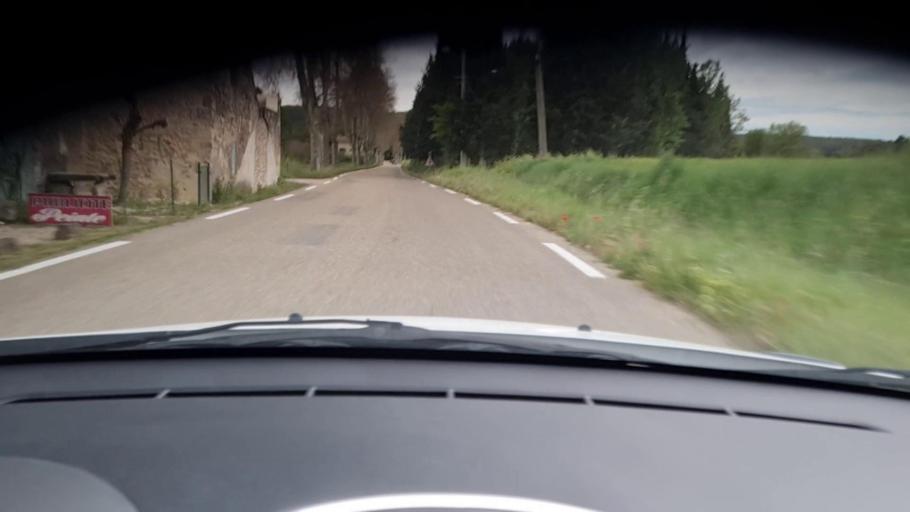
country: FR
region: Languedoc-Roussillon
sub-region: Departement du Gard
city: Blauzac
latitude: 43.9525
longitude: 4.3793
